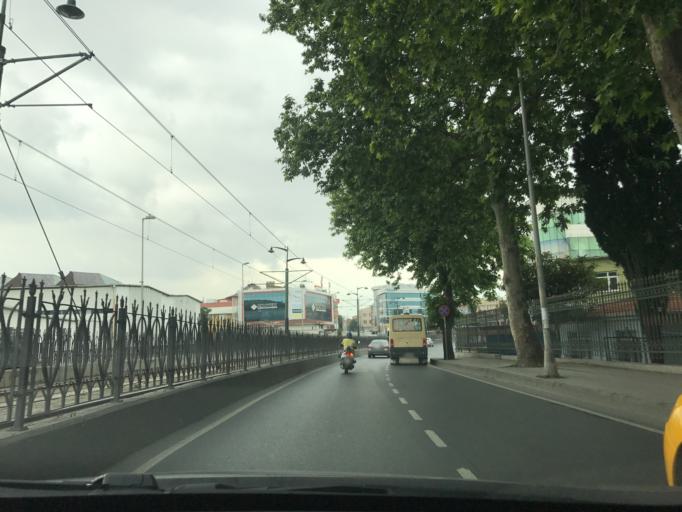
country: TR
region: Istanbul
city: Istanbul
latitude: 41.0352
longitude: 28.9256
